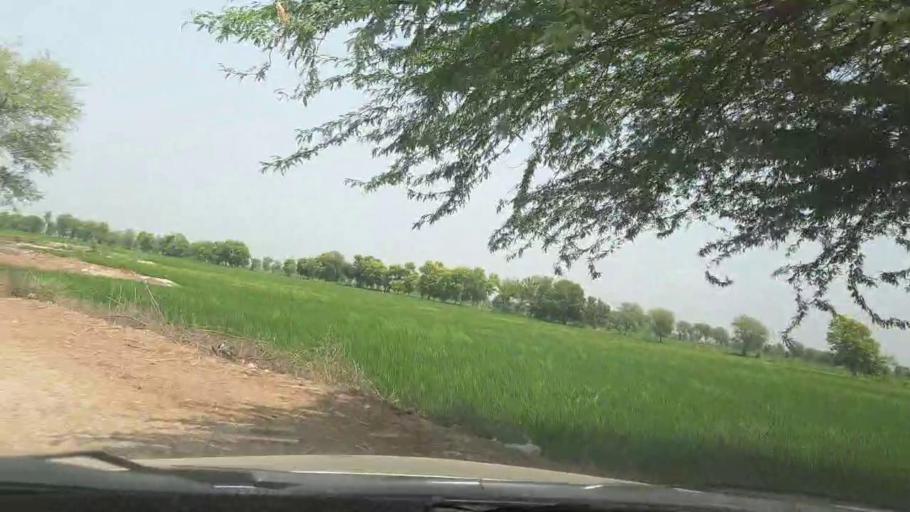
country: PK
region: Sindh
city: Ratodero
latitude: 27.7309
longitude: 68.2971
